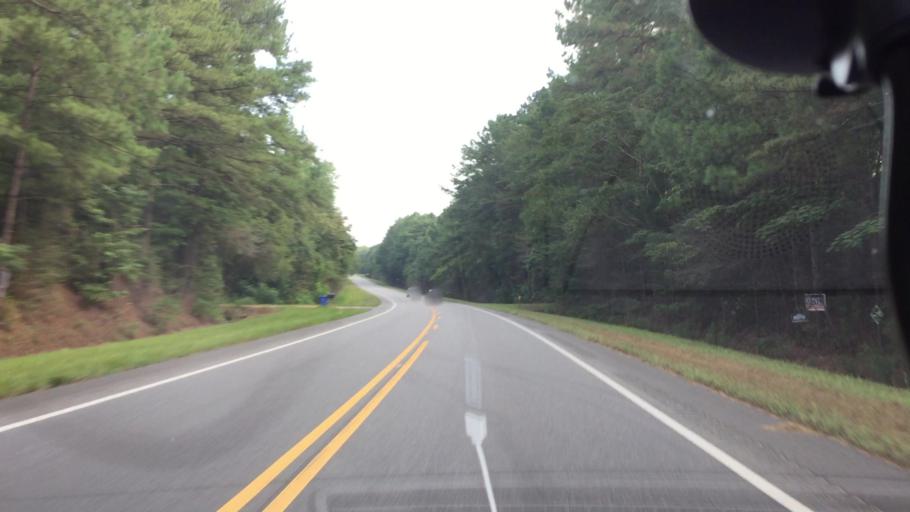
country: US
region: Alabama
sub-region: Pike County
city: Brundidge
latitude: 31.5954
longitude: -85.9457
